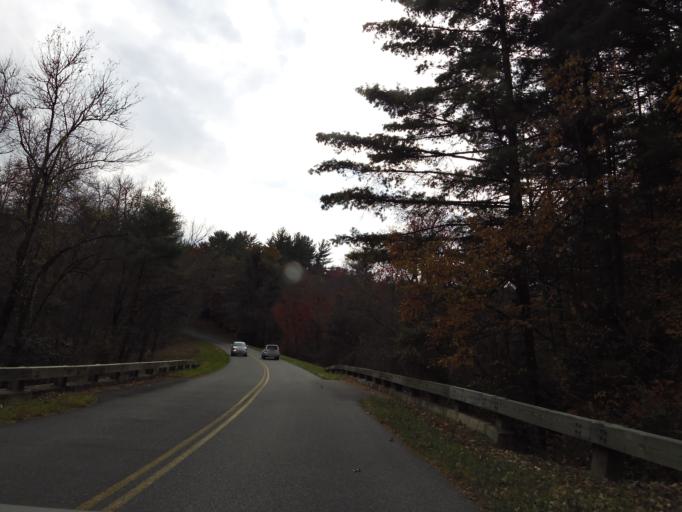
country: US
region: Virginia
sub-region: City of Galax
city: Galax
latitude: 36.5826
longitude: -80.8568
